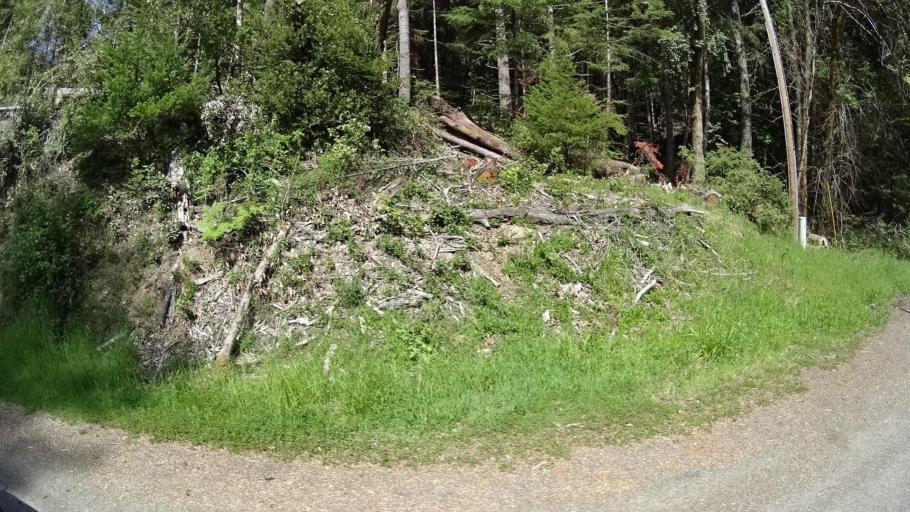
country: US
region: California
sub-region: Humboldt County
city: Redway
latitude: 40.3459
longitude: -123.7103
